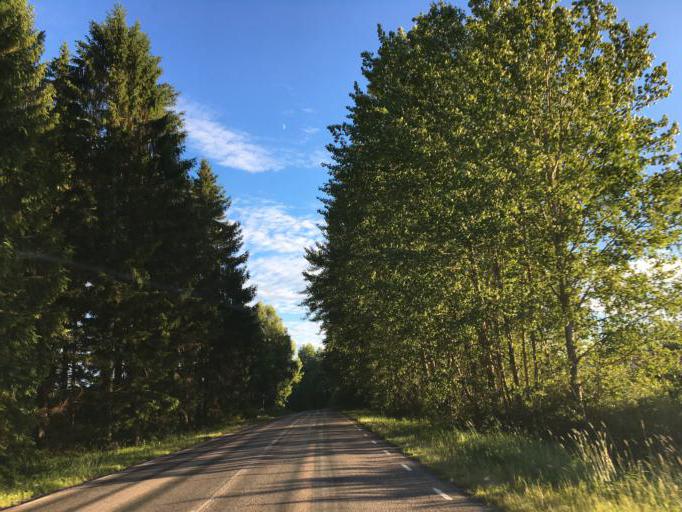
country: SE
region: Vaestmanland
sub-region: Vasteras
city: Vasteras
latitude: 59.5385
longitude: 16.5383
